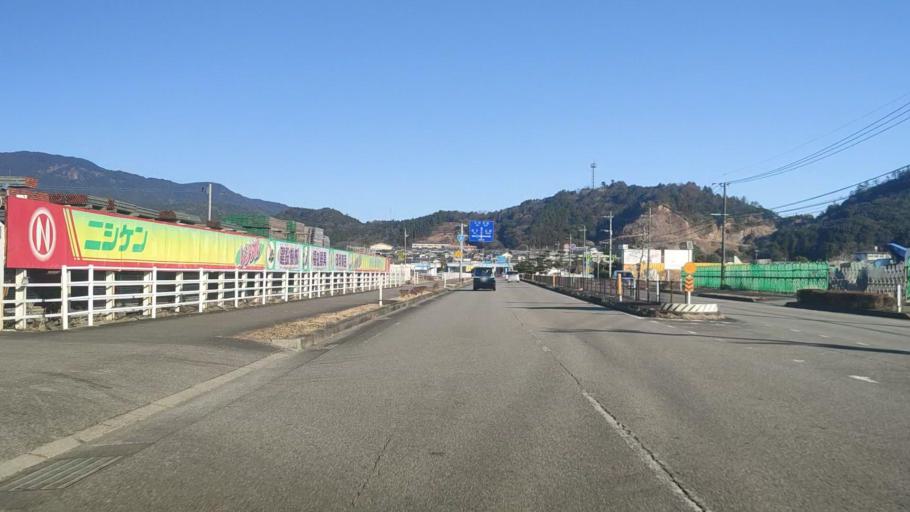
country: JP
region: Miyazaki
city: Nobeoka
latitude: 32.6063
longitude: 131.6829
